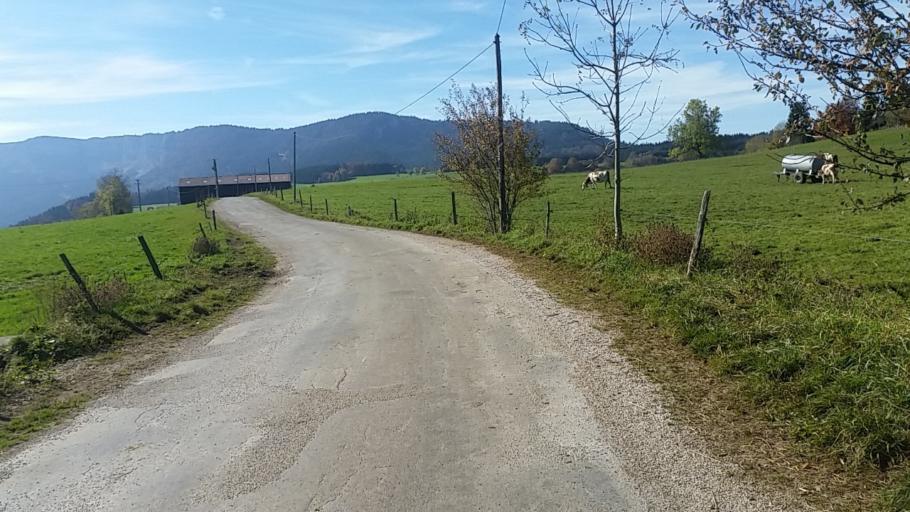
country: FR
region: Franche-Comte
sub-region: Departement du Doubs
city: Jougne
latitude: 46.7669
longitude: 6.3959
